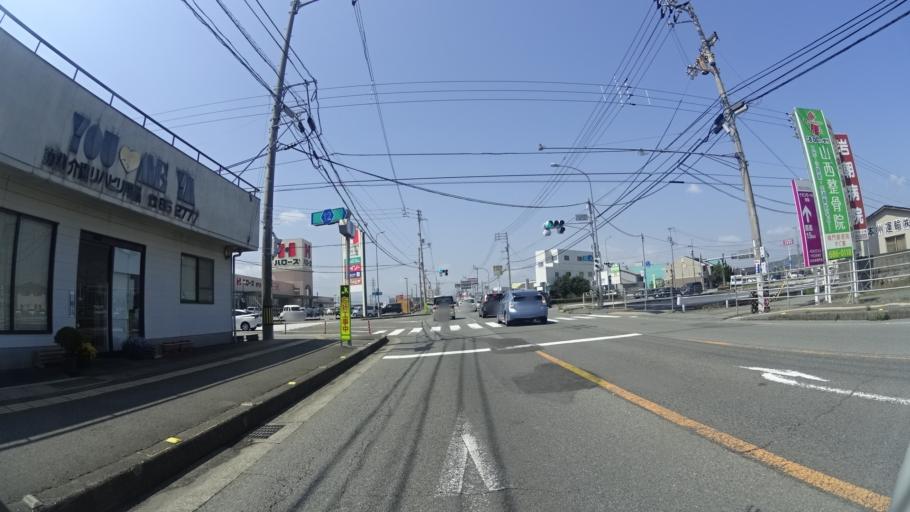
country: JP
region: Tokushima
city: Narutocho-mitsuishi
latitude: 34.1671
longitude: 134.5999
